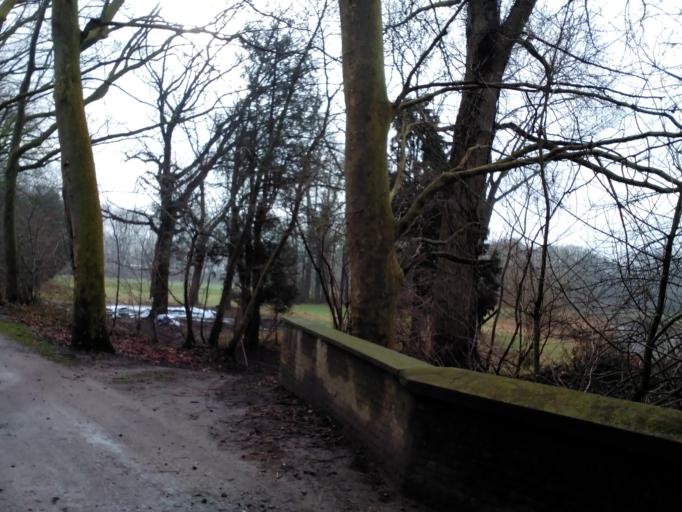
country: BE
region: Wallonia
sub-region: Province du Brabant Wallon
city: Grez-Doiceau
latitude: 50.7387
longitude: 4.6482
